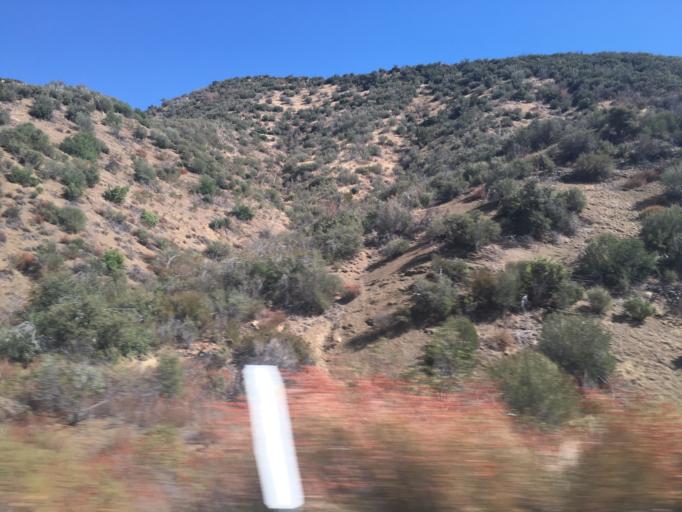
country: US
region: California
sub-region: Ventura County
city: Ojai
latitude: 34.5713
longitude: -119.2593
